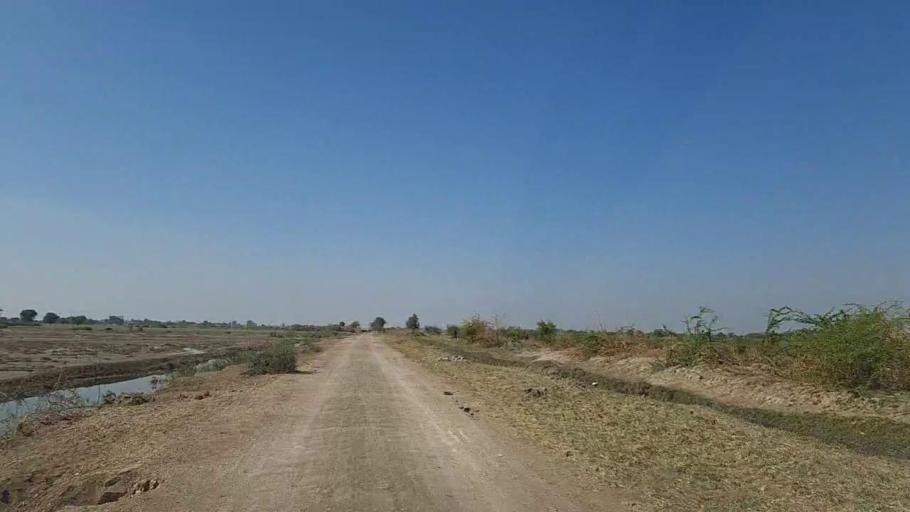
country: PK
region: Sindh
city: Pithoro
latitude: 25.4258
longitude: 69.3491
